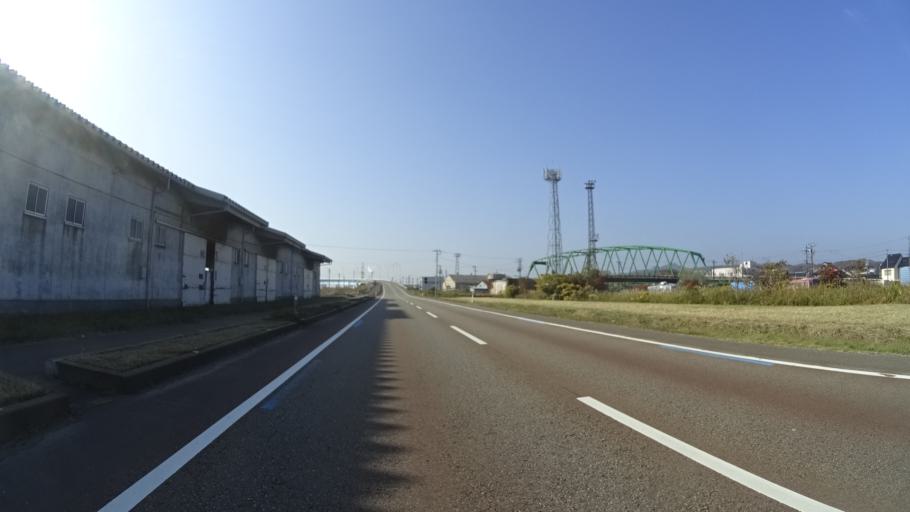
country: JP
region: Toyama
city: Nishishinminato
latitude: 36.7925
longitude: 137.0609
